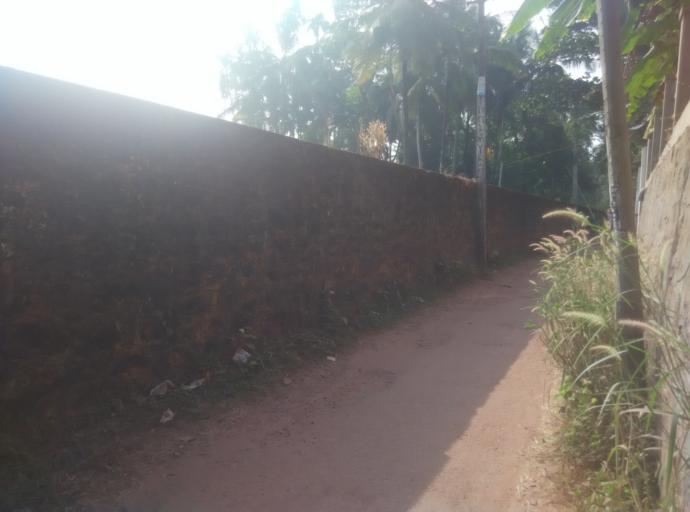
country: IN
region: Kerala
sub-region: Kozhikode
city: Kunnamangalam
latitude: 11.2935
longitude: 75.8297
